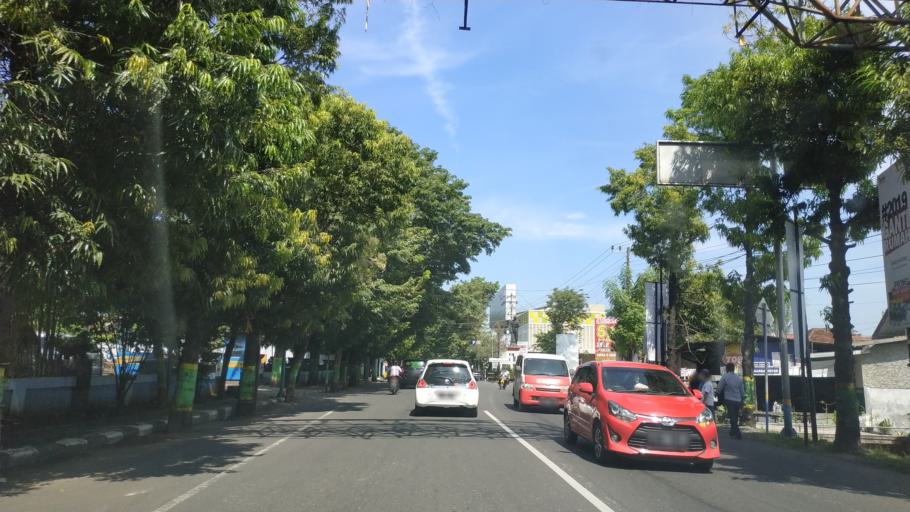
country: ID
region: Central Java
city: Baran
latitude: -6.7525
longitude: 111.0517
